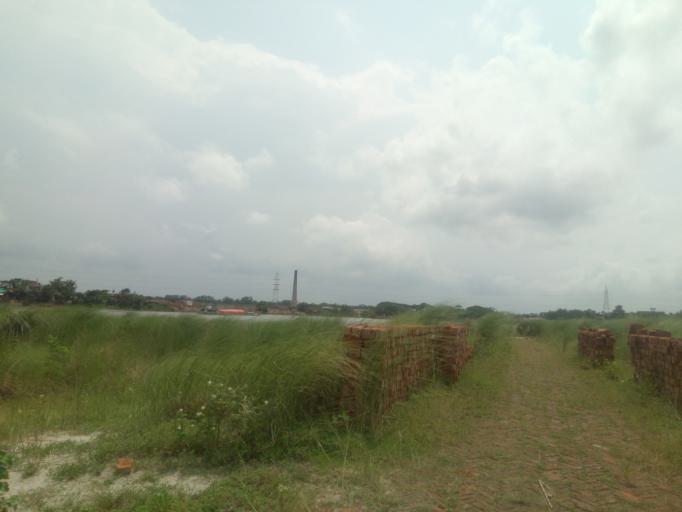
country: BD
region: Dhaka
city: Azimpur
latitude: 23.7504
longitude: 90.3323
